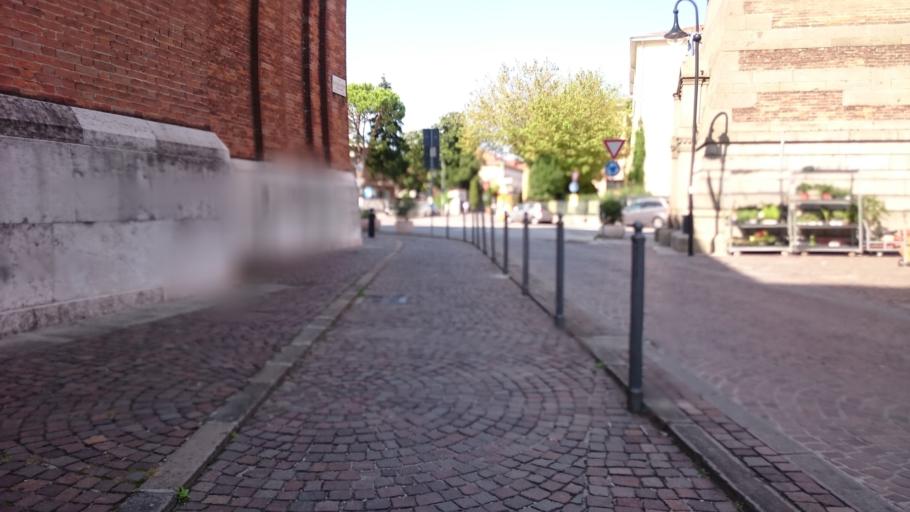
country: IT
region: Veneto
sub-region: Provincia di Padova
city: Padova
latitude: 45.4218
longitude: 11.8864
